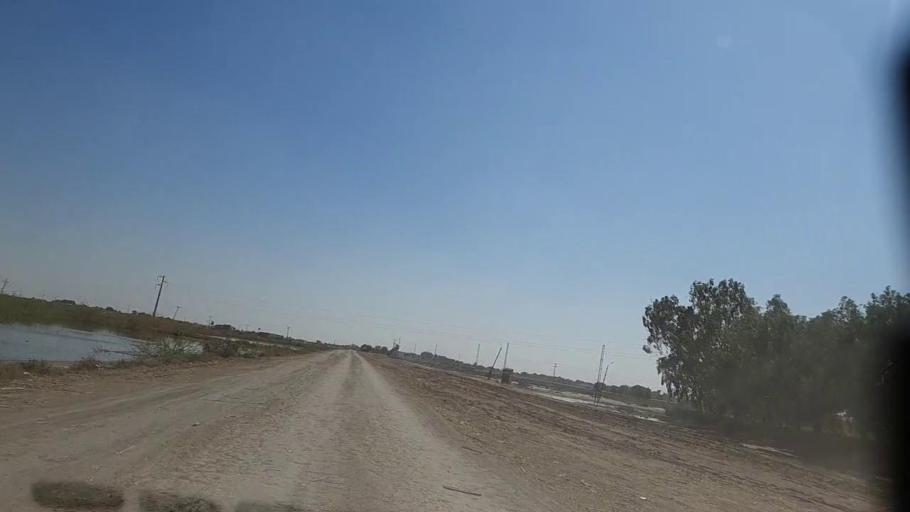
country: PK
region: Sindh
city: Digri
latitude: 25.1603
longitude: 69.0417
